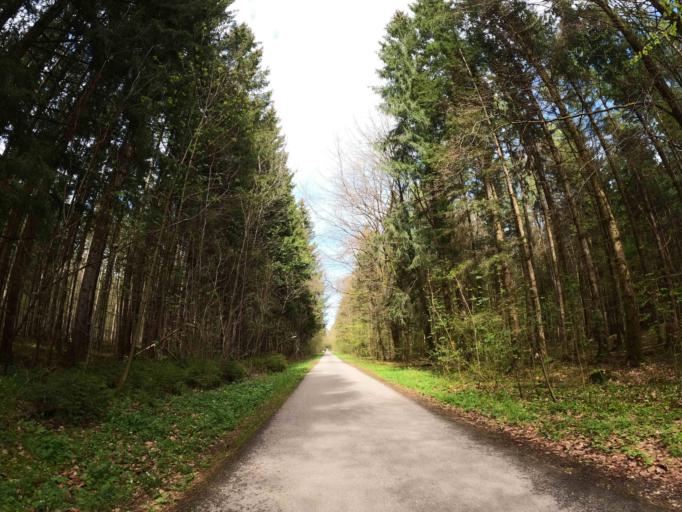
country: DE
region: Bavaria
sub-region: Upper Bavaria
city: Strasslach-Dingharting
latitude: 48.0143
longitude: 11.5244
